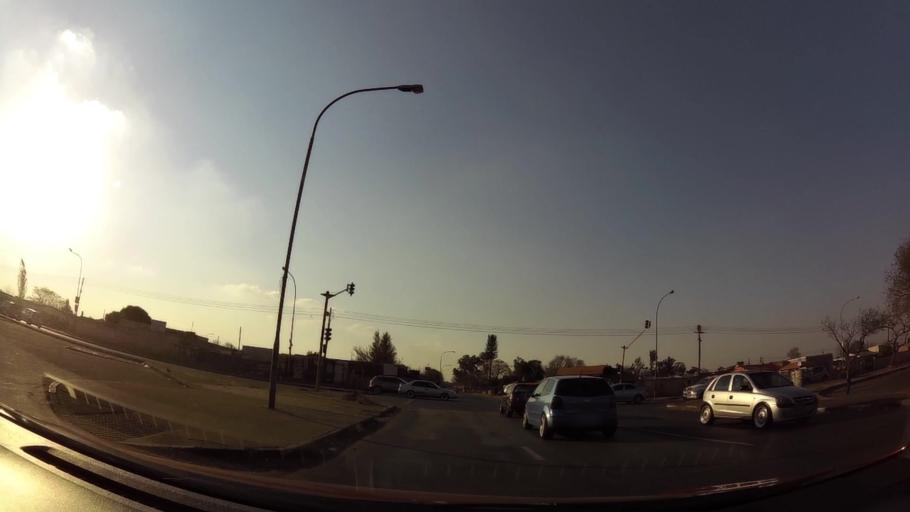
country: ZA
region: Gauteng
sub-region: City of Johannesburg Metropolitan Municipality
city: Soweto
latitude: -26.2918
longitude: 27.8953
